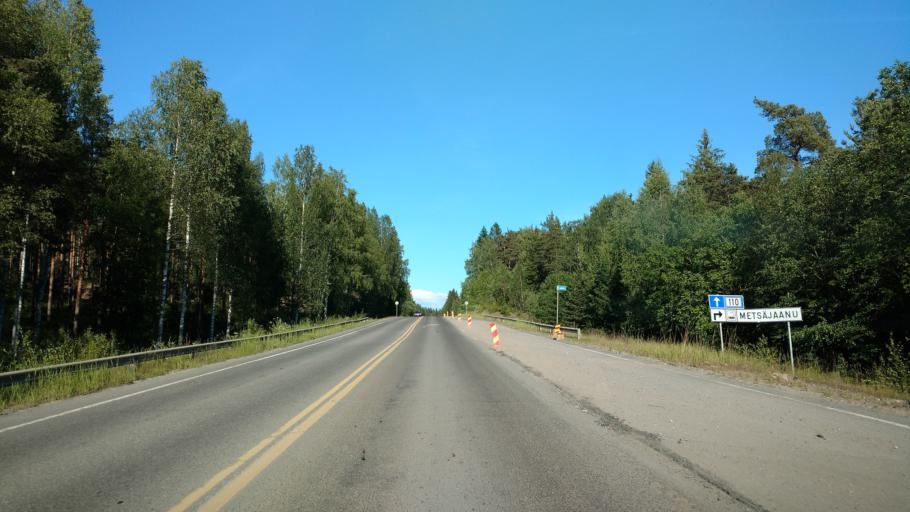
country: FI
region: Varsinais-Suomi
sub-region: Salo
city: Salo
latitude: 60.3819
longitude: 23.1835
